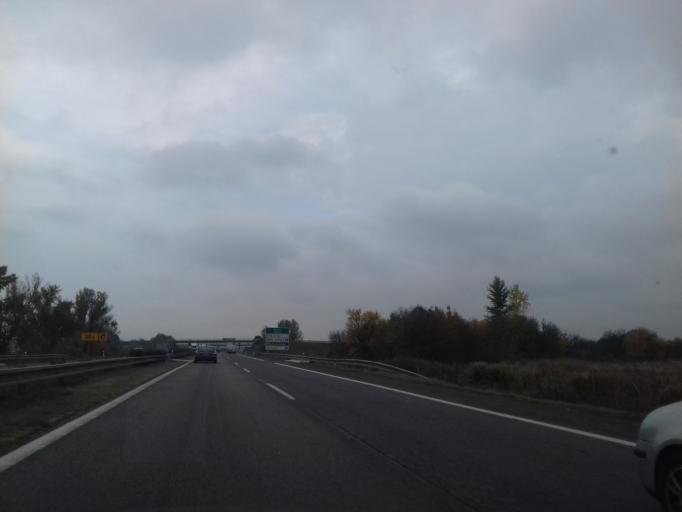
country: SK
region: Bratislavsky
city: Stupava
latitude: 48.2416
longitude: 17.0160
